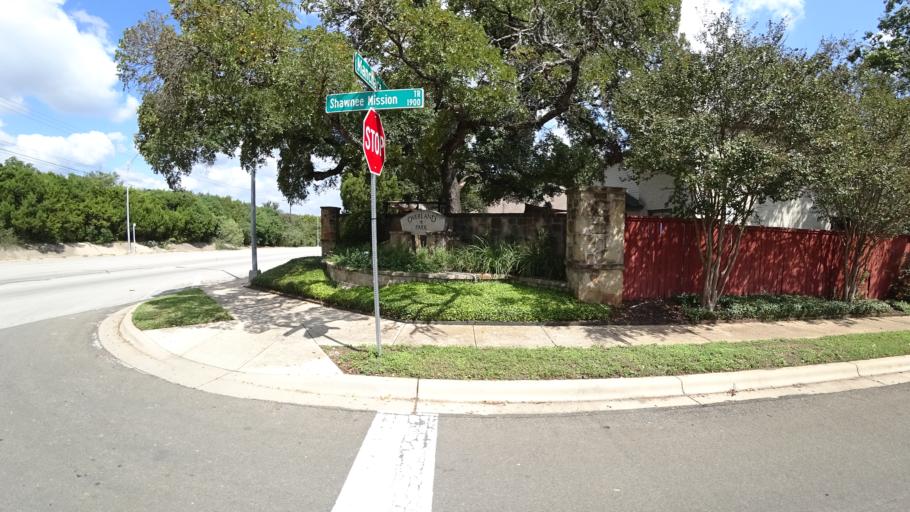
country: US
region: Texas
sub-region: Travis County
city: Manchaca
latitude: 30.1878
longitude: -97.8148
